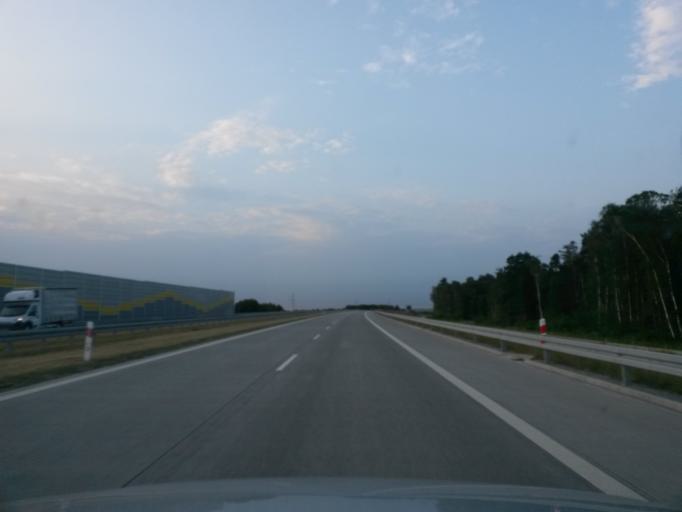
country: PL
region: Lodz Voivodeship
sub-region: Powiat sieradzki
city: Brzeznio
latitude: 51.4570
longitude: 18.6505
